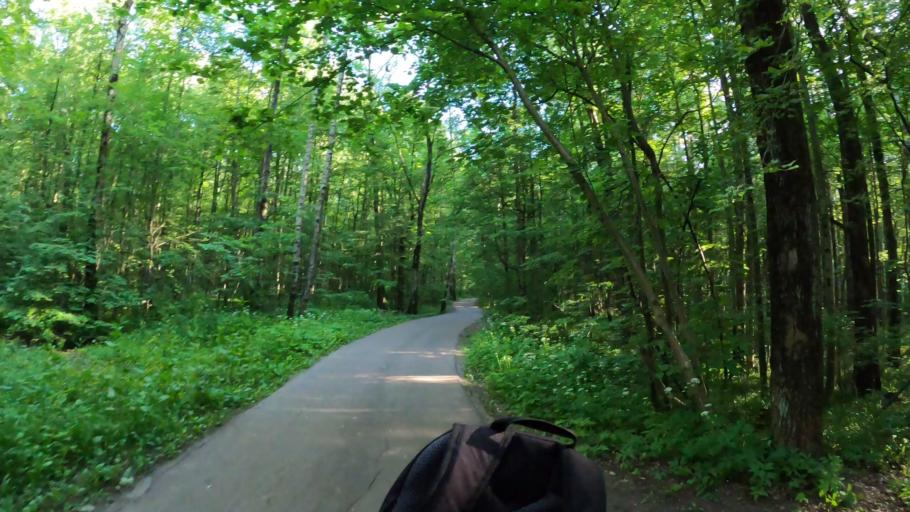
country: RU
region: Moscow
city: Zyuzino
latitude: 55.6195
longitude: 37.5608
